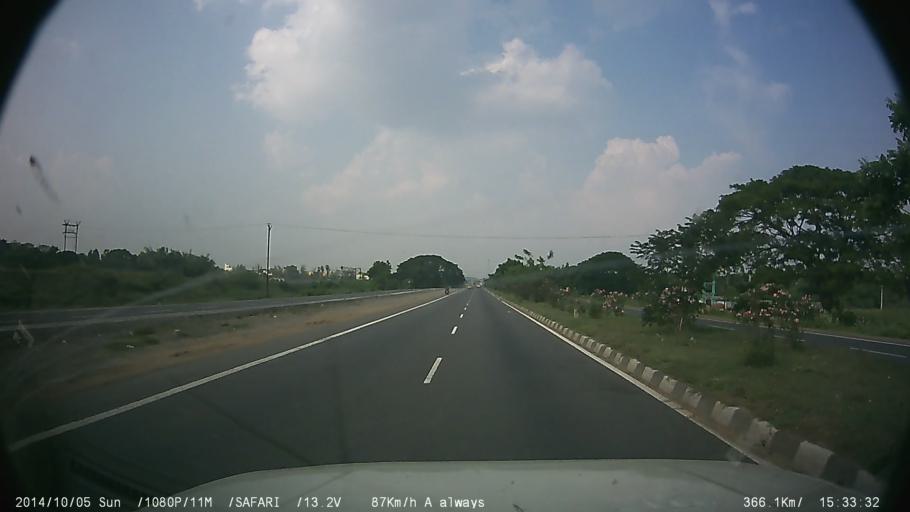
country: IN
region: Tamil Nadu
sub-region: Kancheepuram
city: Chengalpattu
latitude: 12.6931
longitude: 79.9647
